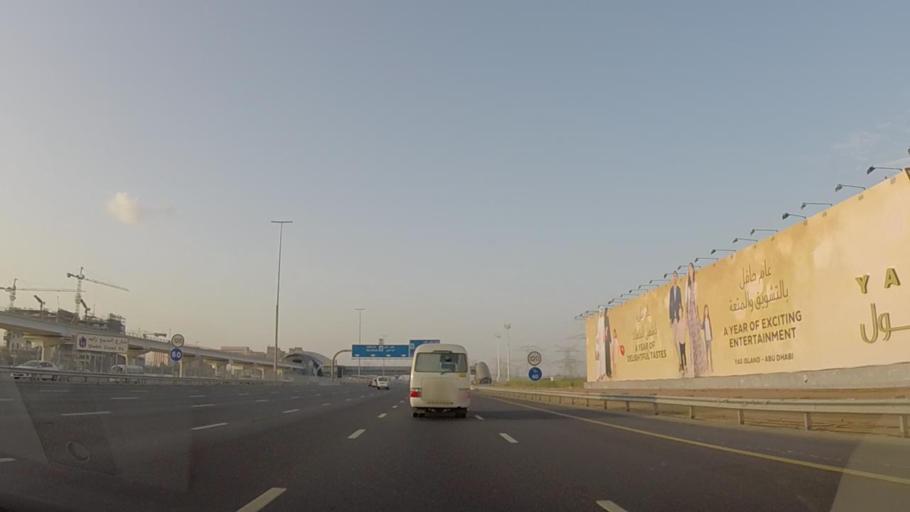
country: AE
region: Dubai
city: Dubai
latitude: 25.0498
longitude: 55.1193
